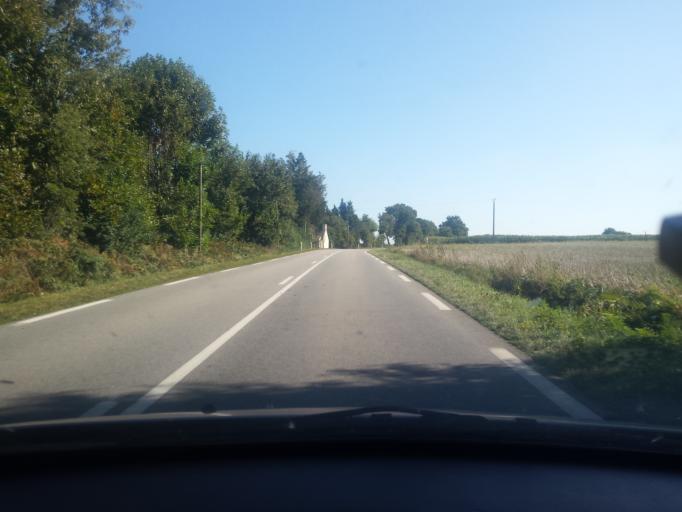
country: FR
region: Brittany
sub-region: Departement du Morbihan
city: Saint-Thuriau
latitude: 48.0208
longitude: -2.9102
